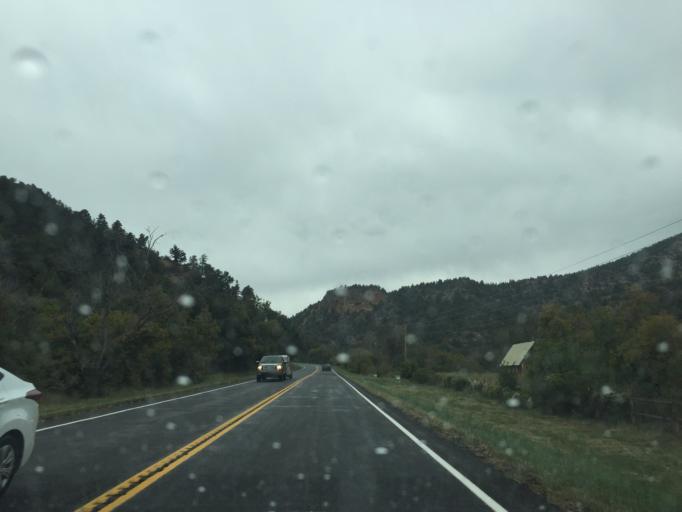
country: US
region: Utah
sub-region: Kane County
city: Kanab
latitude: 37.3483
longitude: -112.5994
